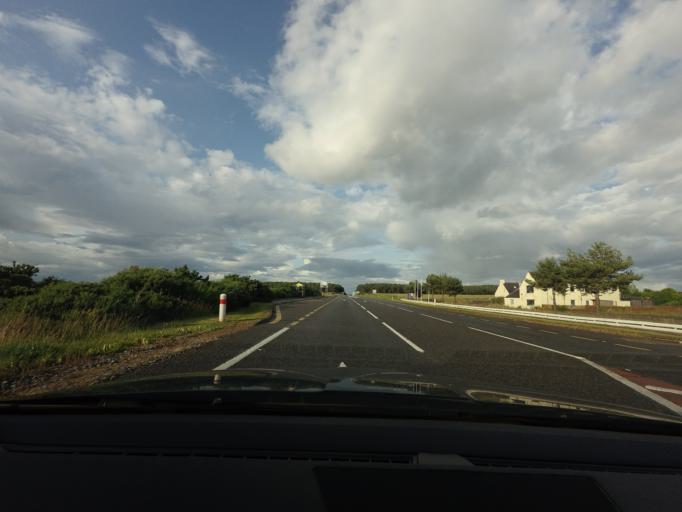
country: GB
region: Scotland
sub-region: Highland
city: Nairn
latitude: 57.5448
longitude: -4.0039
